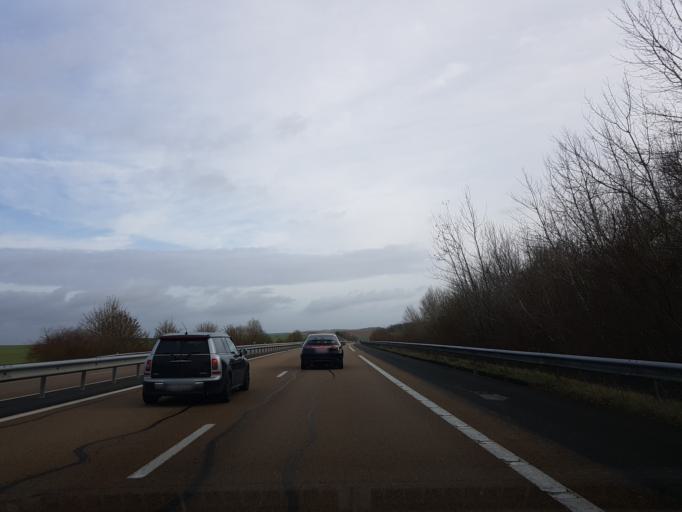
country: FR
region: Champagne-Ardenne
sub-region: Departement de l'Aube
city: Aix-en-Othe
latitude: 48.2682
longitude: 3.6966
